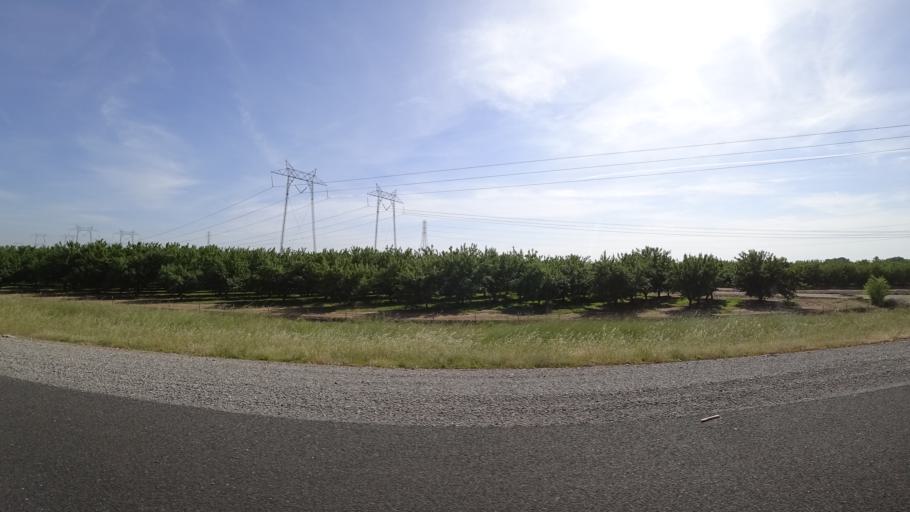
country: US
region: California
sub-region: Butte County
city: Thermalito
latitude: 39.6054
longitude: -121.6697
